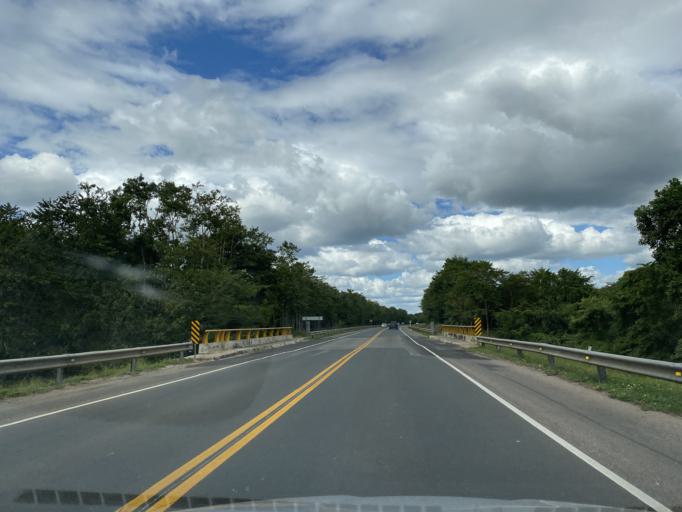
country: DO
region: Santo Domingo
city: Guerra
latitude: 18.5921
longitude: -69.7704
